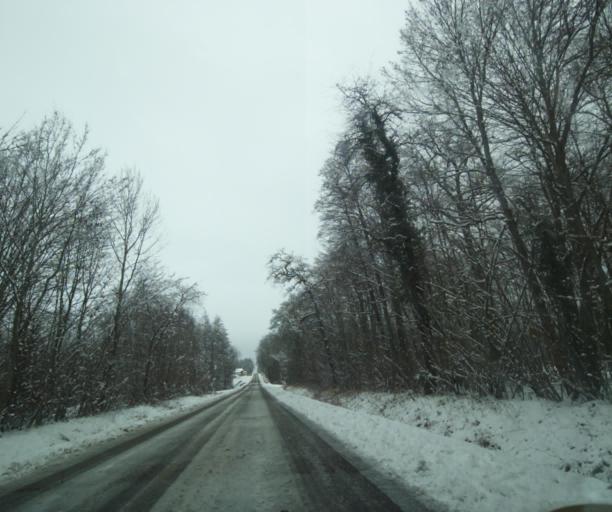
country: FR
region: Champagne-Ardenne
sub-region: Departement de la Haute-Marne
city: Montier-en-Der
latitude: 48.5220
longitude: 4.7479
